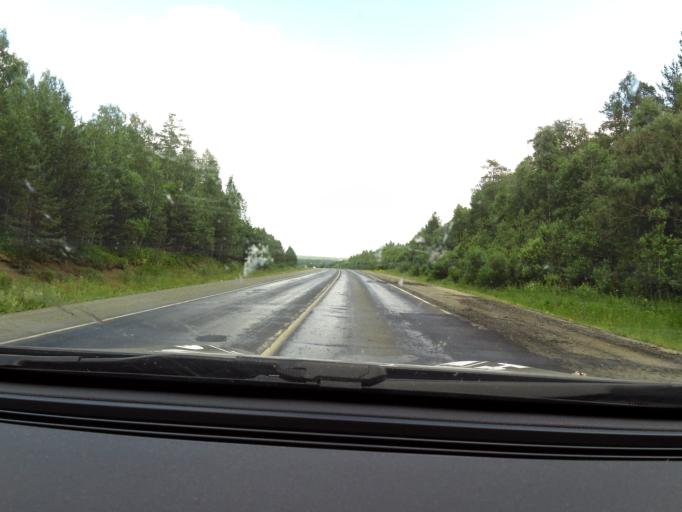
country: RU
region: Sverdlovsk
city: Bisert'
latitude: 56.8343
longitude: 58.8940
